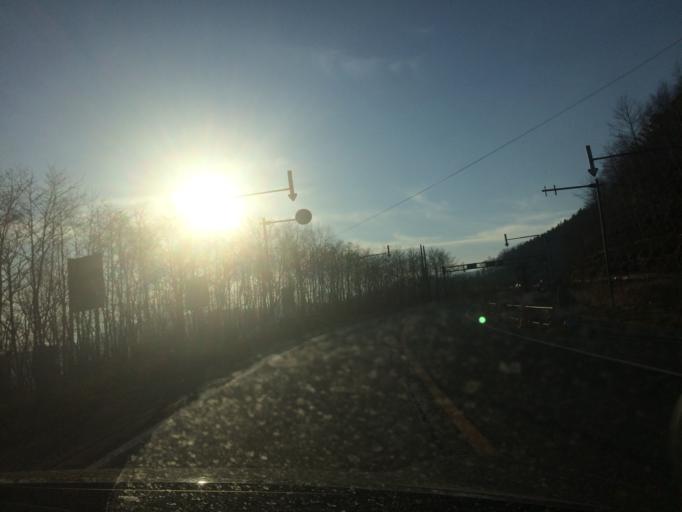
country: JP
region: Hokkaido
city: Otofuke
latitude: 42.9742
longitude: 142.8014
